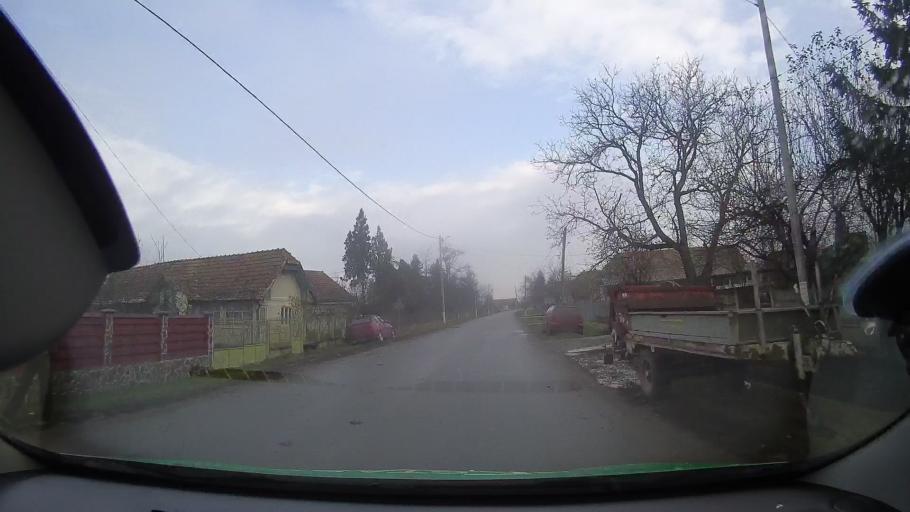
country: RO
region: Alba
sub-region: Comuna Noslac
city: Noslac
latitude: 46.4202
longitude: 23.9804
